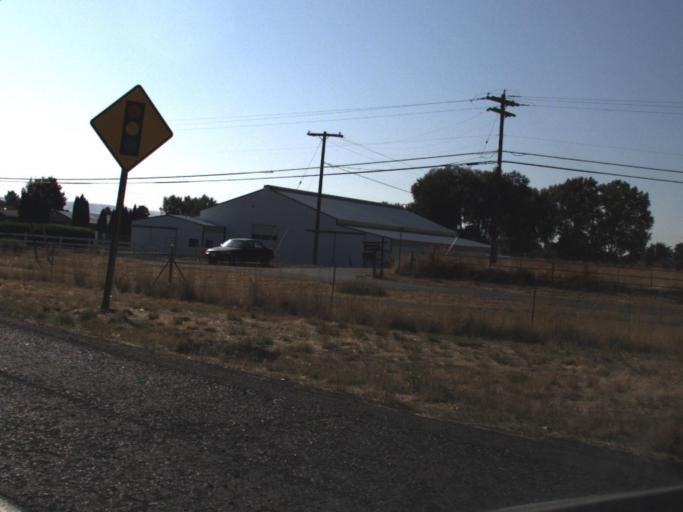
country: US
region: Washington
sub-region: Walla Walla County
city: College Place
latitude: 46.0266
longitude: -118.3885
